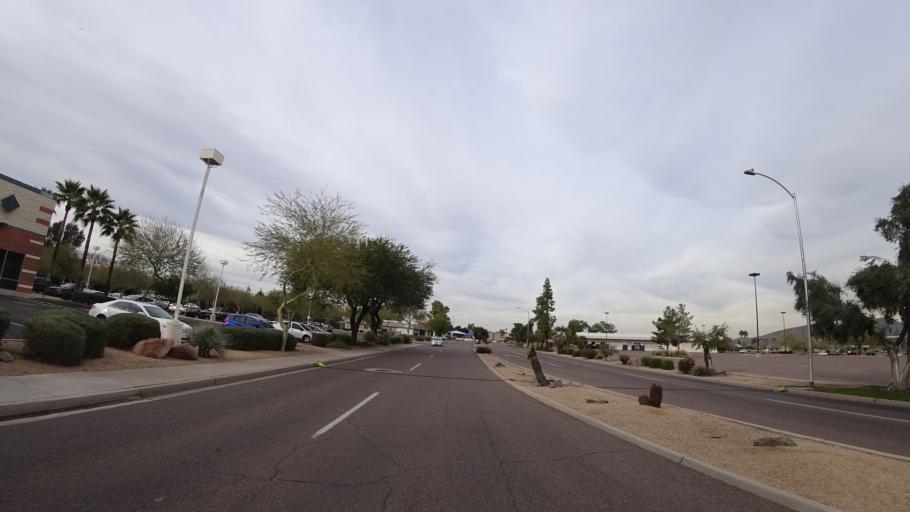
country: US
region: Arizona
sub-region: Maricopa County
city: Glendale
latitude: 33.5770
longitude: -112.1253
